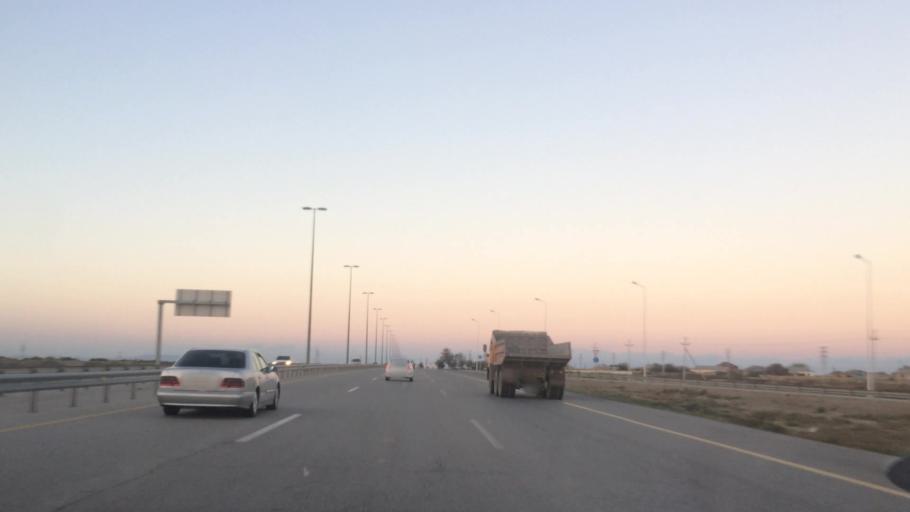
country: AZ
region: Baki
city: Qobustan
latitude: 39.9834
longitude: 49.4247
